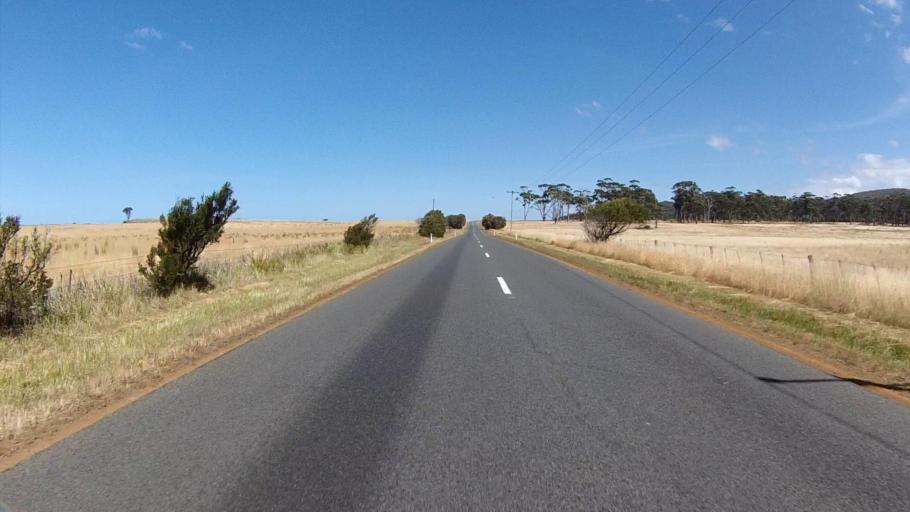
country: AU
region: Tasmania
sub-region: Sorell
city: Sorell
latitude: -42.2068
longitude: 148.0415
